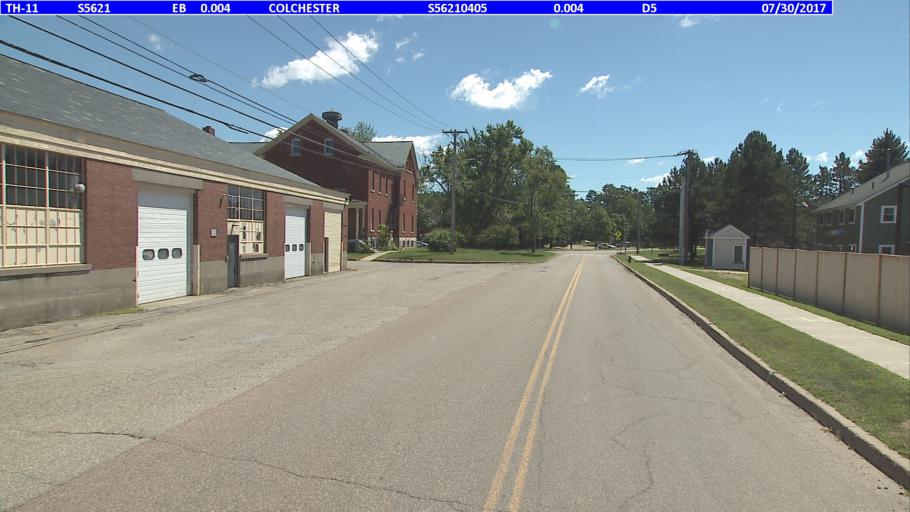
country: US
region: Vermont
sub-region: Chittenden County
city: Winooski
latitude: 44.5029
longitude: -73.1528
